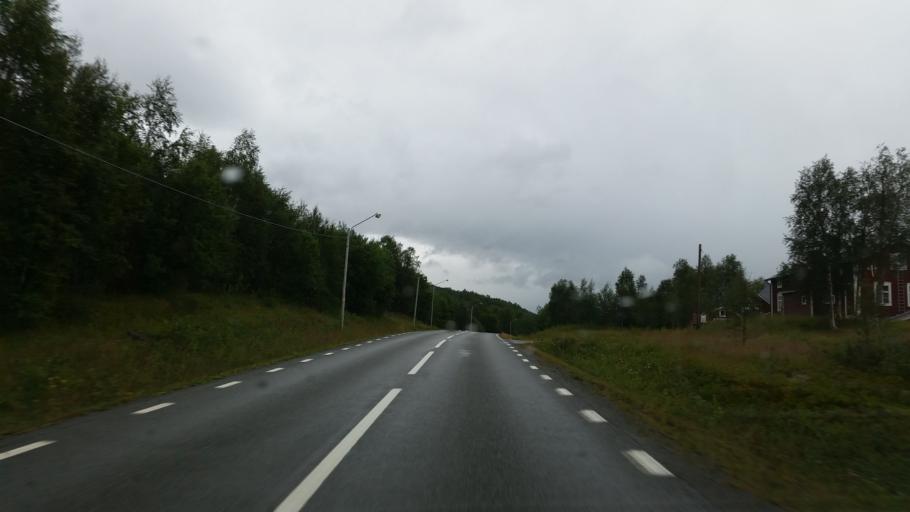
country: NO
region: Nordland
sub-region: Rana
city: Mo i Rana
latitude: 65.8664
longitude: 15.0177
